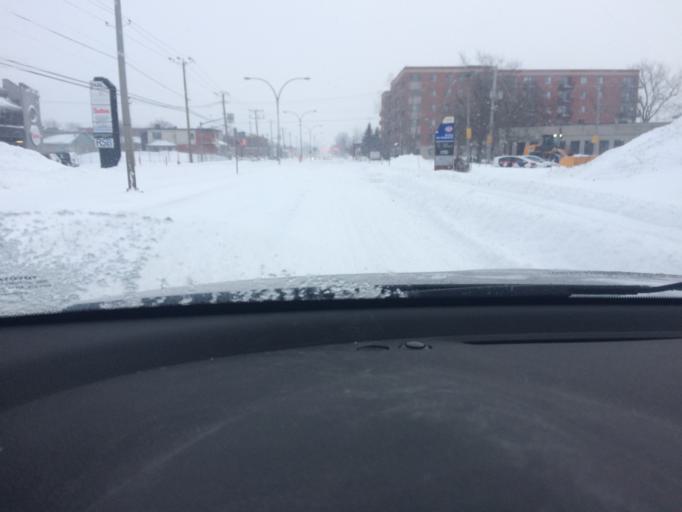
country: CA
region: Quebec
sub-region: Monteregie
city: Brossard
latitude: 45.4708
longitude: -73.4663
